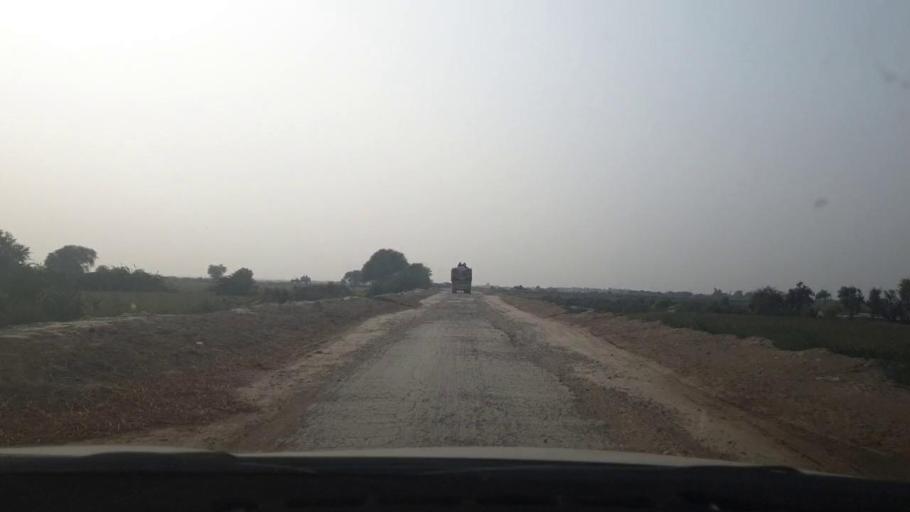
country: PK
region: Sindh
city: Bulri
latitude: 24.7856
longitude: 68.4222
